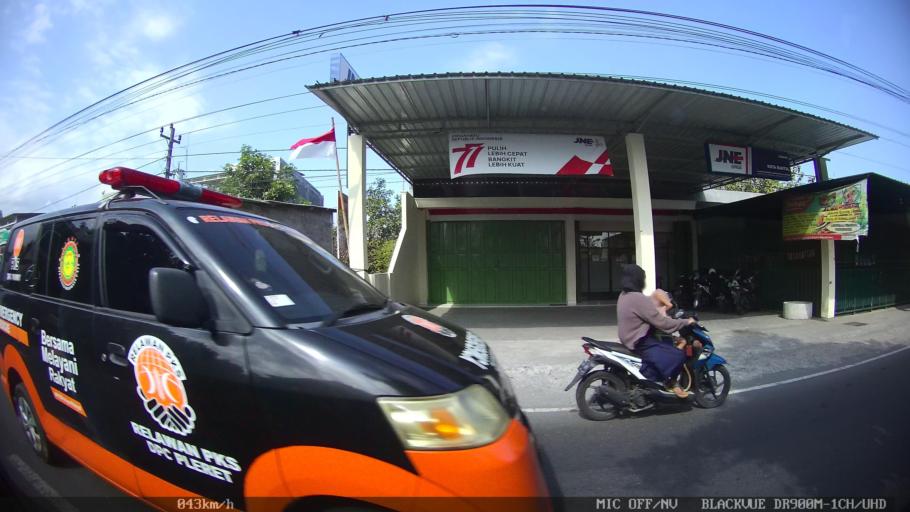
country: ID
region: Daerah Istimewa Yogyakarta
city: Sewon
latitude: -7.8540
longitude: 110.3902
